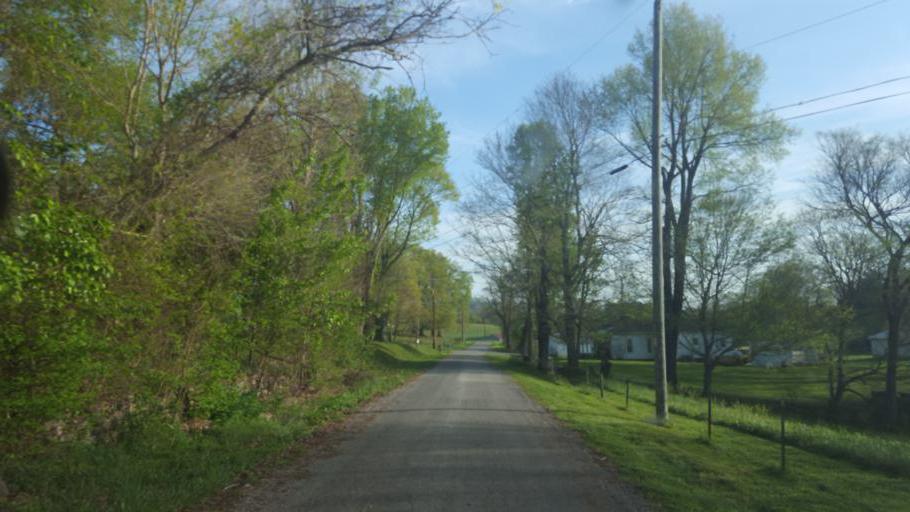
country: US
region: Kentucky
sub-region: Hart County
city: Munfordville
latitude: 37.2596
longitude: -85.8872
